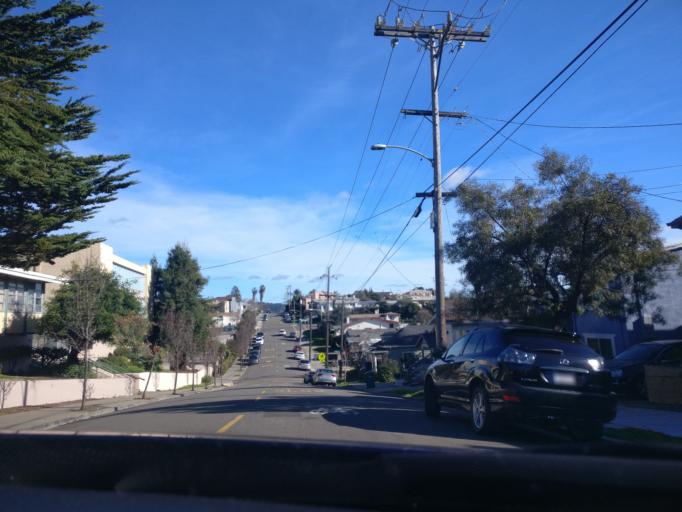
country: US
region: California
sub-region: Alameda County
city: Piedmont
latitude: 37.8031
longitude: -122.2297
